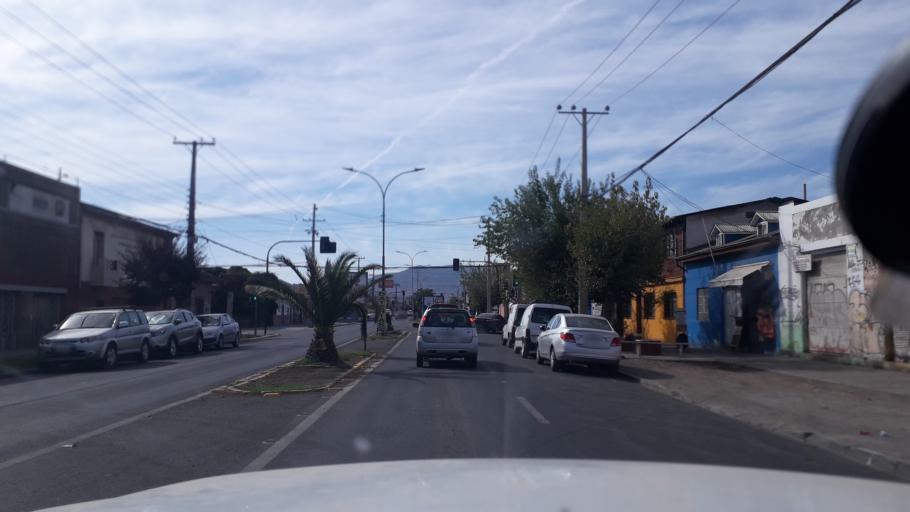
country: CL
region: Valparaiso
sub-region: Provincia de San Felipe
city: San Felipe
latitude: -32.7517
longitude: -70.7305
